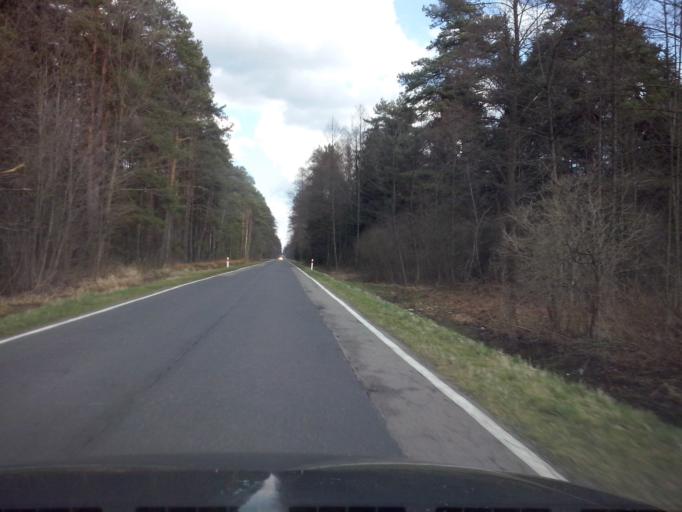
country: PL
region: Subcarpathian Voivodeship
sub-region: Powiat nizanski
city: Harasiuki
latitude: 50.4981
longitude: 22.5289
